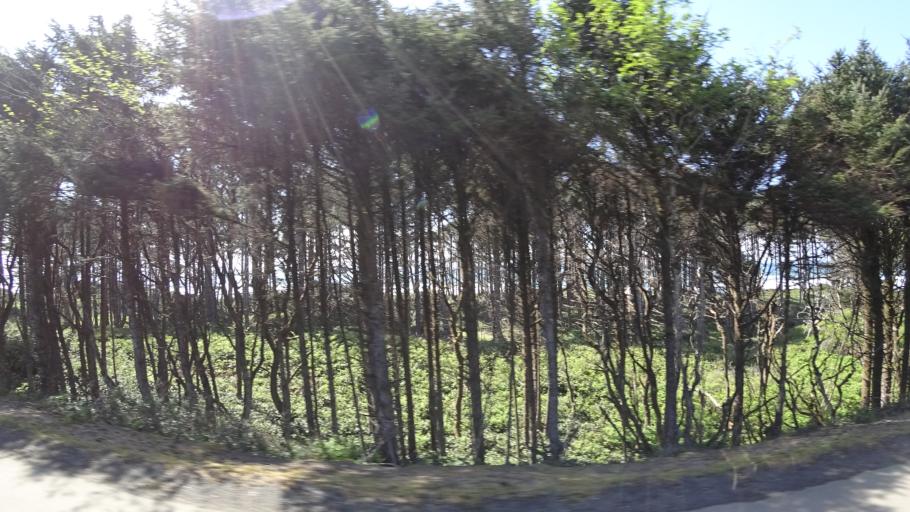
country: US
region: Oregon
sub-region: Lincoln County
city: Newport
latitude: 44.6984
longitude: -124.0620
